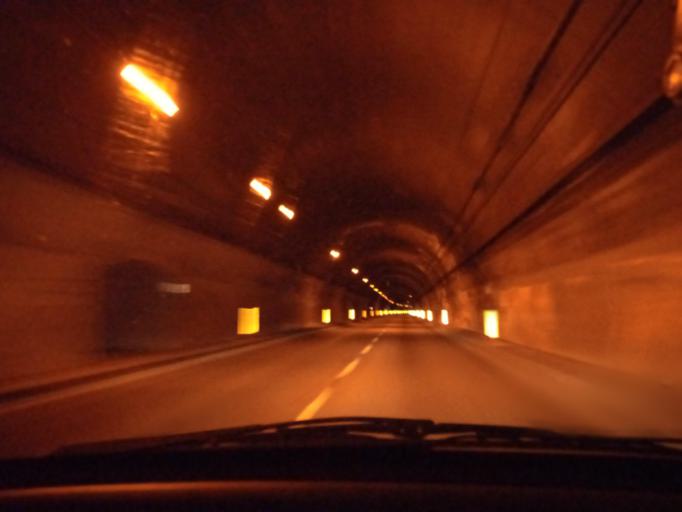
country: IT
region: Sicily
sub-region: Messina
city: Naso
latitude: 38.1455
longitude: 14.7982
